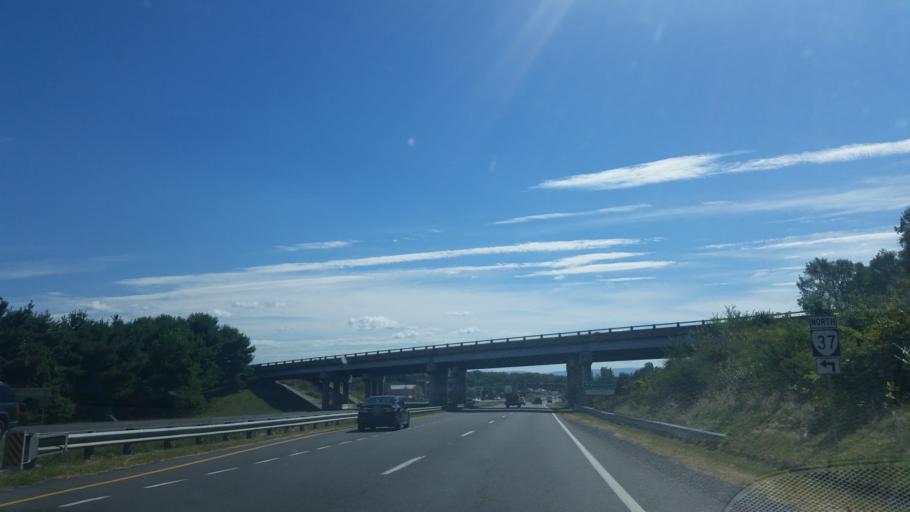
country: US
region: Virginia
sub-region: City of Winchester
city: Winchester
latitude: 39.2109
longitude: -78.1826
